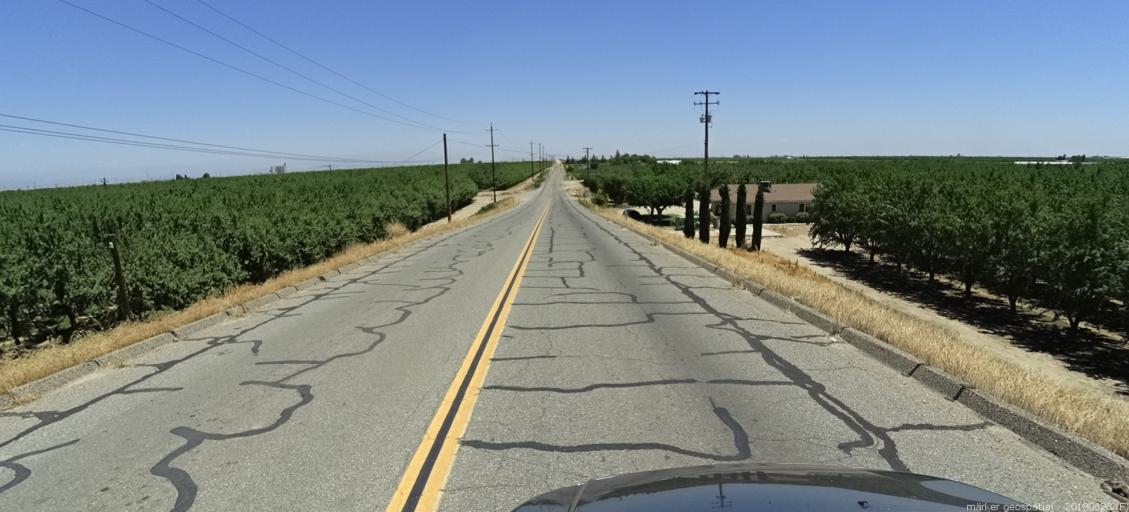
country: US
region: California
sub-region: Madera County
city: Parksdale
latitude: 36.9094
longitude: -120.0042
